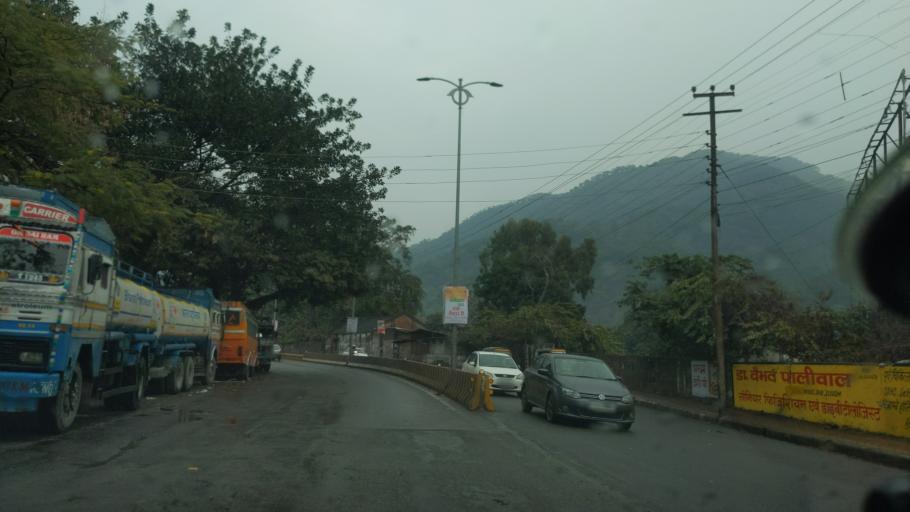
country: IN
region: Uttarakhand
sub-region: Naini Tal
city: Haldwani
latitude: 29.2634
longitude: 79.5443
